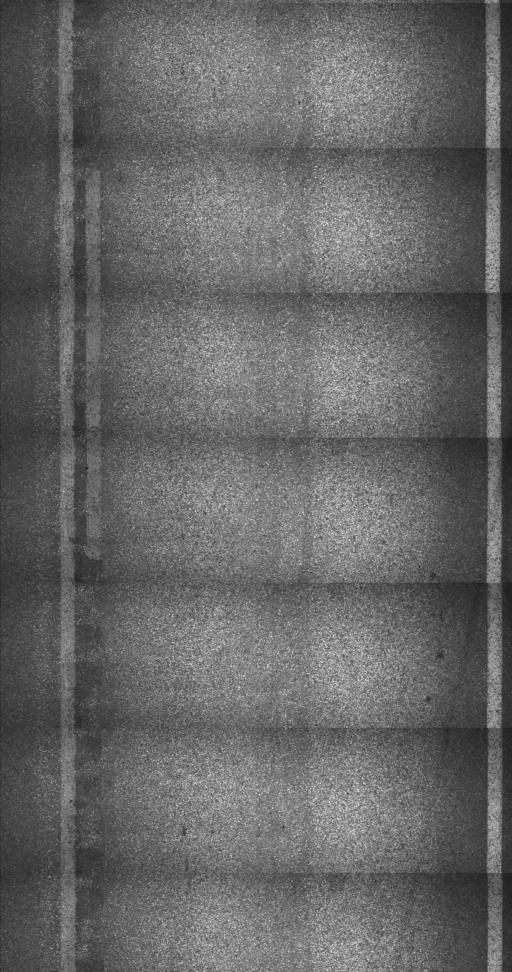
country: US
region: New York
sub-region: Clinton County
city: Cumberland Head
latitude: 44.6939
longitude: -73.3068
